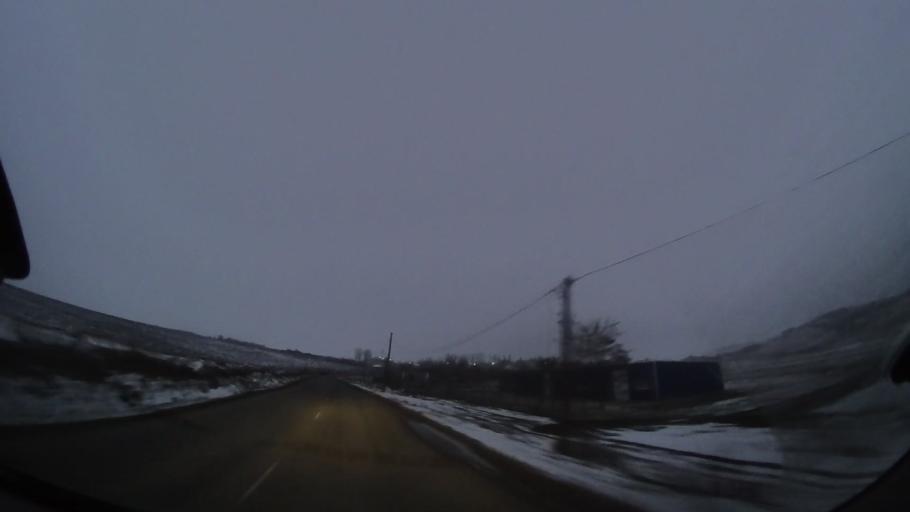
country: RO
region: Vaslui
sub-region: Comuna Dimitrie Cantemir
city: Dimitrie Cantemir
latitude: 46.4939
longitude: 28.0536
